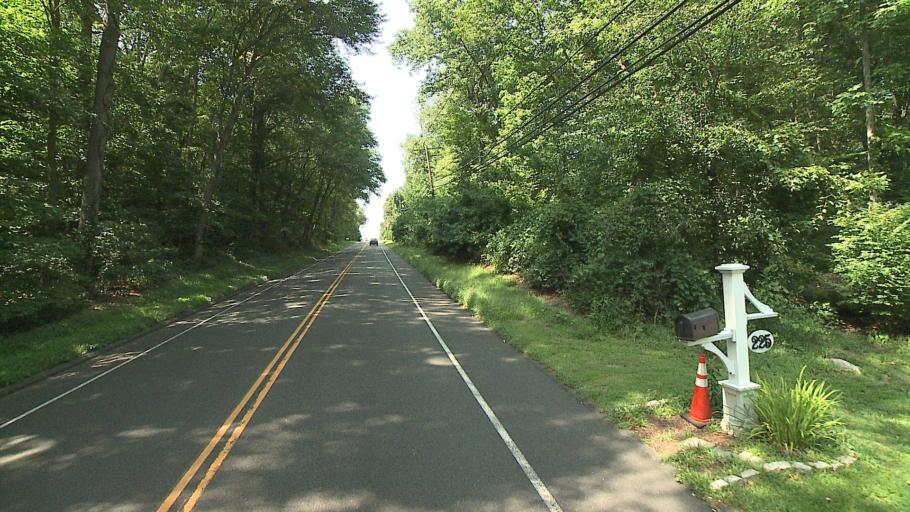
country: US
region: Connecticut
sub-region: Fairfield County
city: Shelton
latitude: 41.3326
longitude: -73.1433
